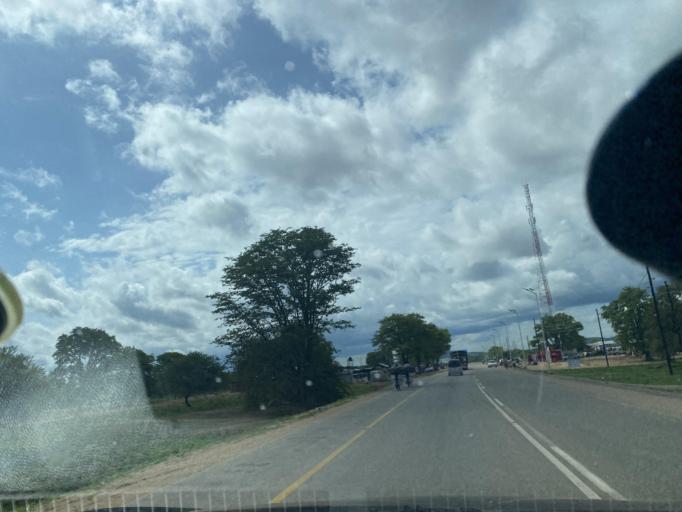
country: ZM
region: Lusaka
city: Kafue
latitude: -15.8524
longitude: 28.2515
